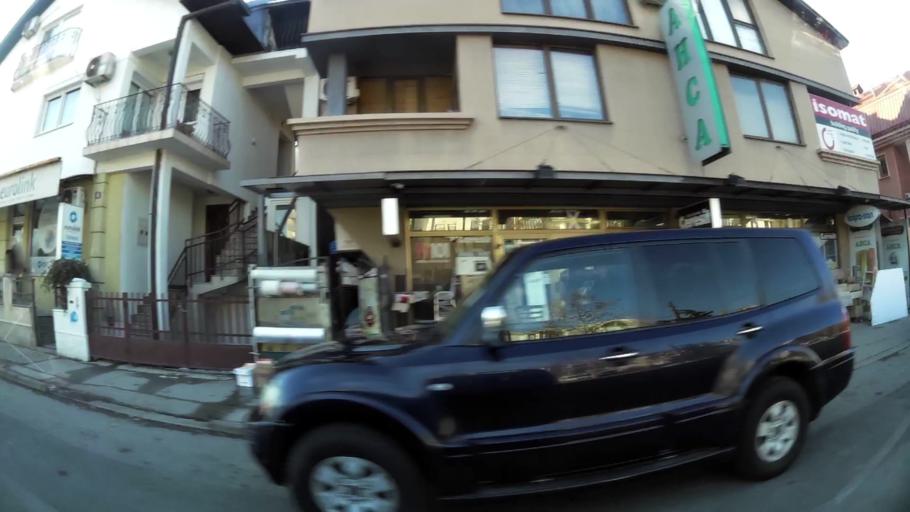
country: MK
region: Karpos
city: Skopje
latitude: 42.0019
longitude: 21.3898
